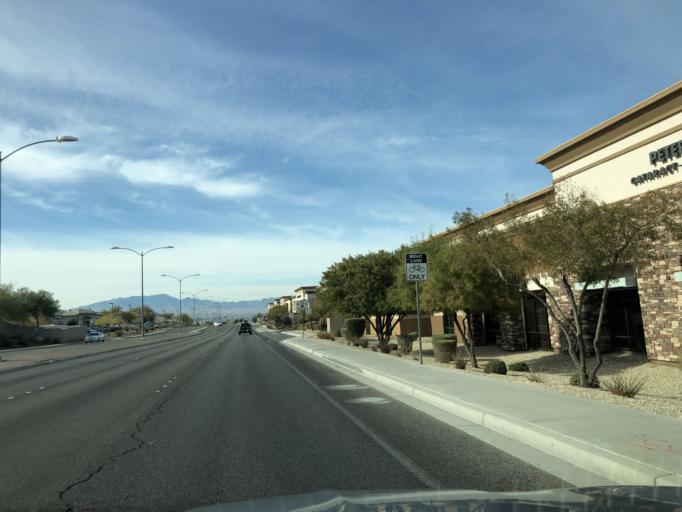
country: US
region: Nevada
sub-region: Clark County
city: Whitney
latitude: 36.0060
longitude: -115.0910
